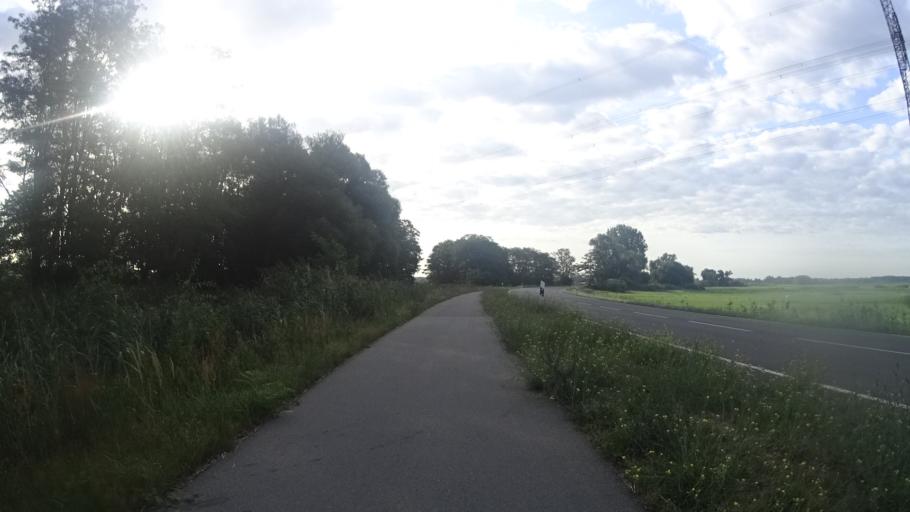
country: DE
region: Brandenburg
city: Premnitz
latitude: 52.5110
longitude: 12.4359
